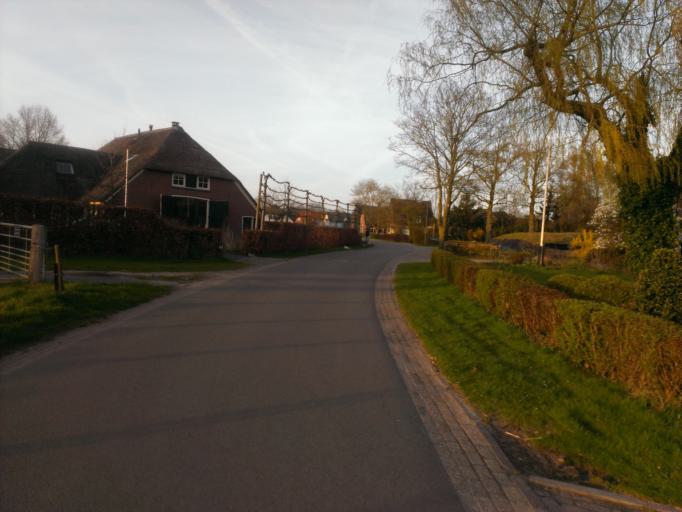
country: NL
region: Gelderland
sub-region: Gemeente Heerde
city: Heerde
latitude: 52.3981
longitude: 6.0585
